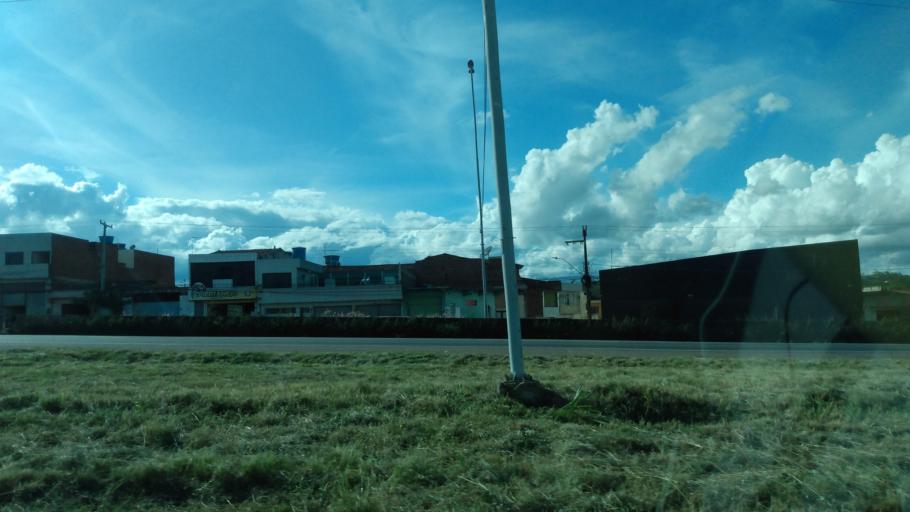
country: ET
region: Oromiya
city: Gore
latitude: 8.1973
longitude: 35.5785
